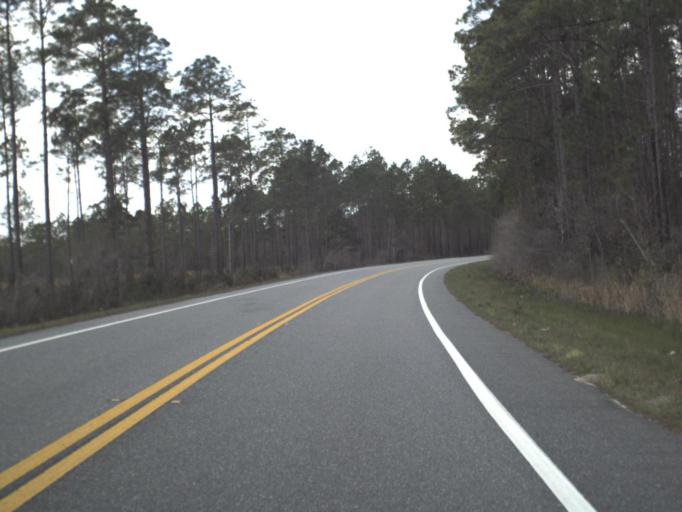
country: US
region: Florida
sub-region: Franklin County
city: Apalachicola
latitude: 29.8466
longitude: -84.9689
